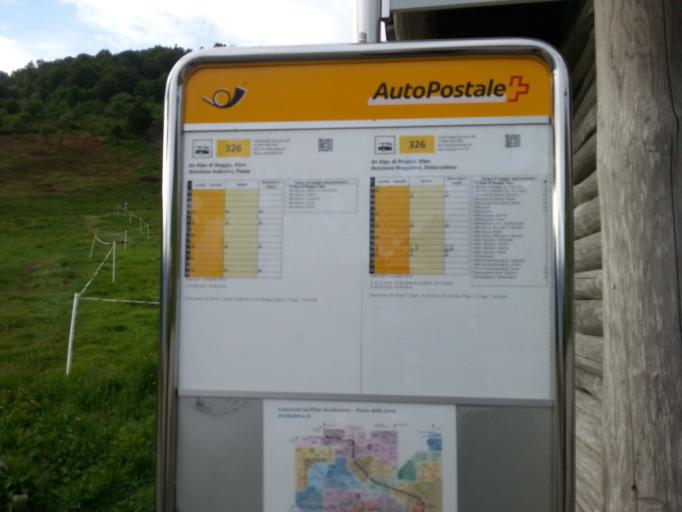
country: CH
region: Ticino
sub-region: Locarno District
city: Magadino
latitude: 46.1107
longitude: 8.8456
